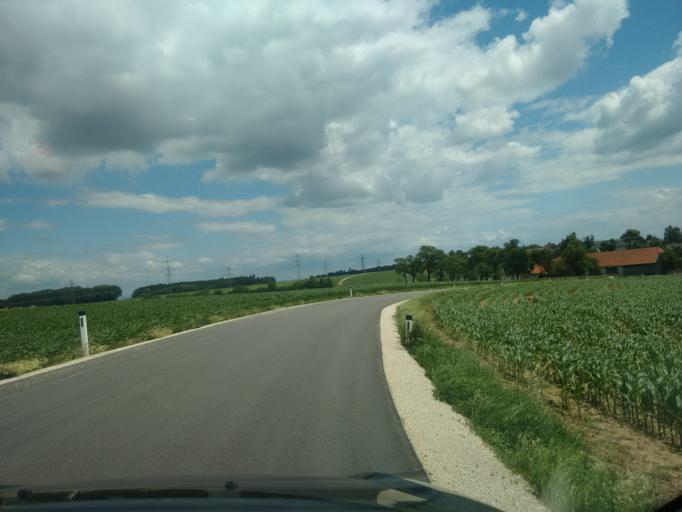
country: AT
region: Upper Austria
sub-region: Politischer Bezirk Steyr-Land
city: Sierning
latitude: 48.0845
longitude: 14.3060
